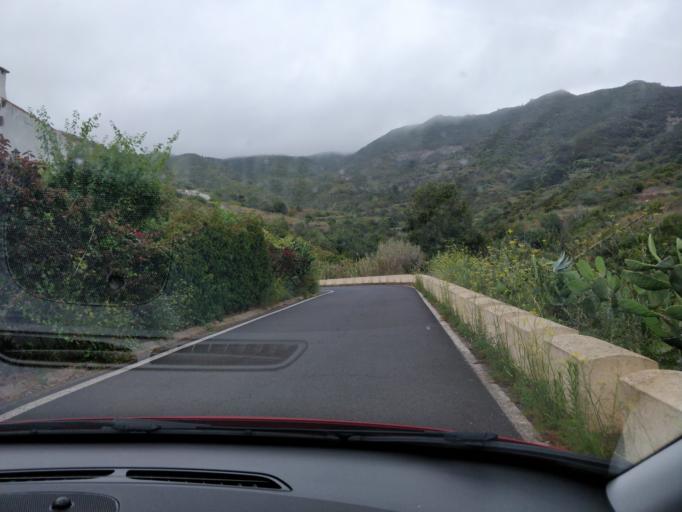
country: ES
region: Canary Islands
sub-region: Provincia de Santa Cruz de Tenerife
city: Santiago del Teide
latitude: 28.3246
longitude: -16.8439
